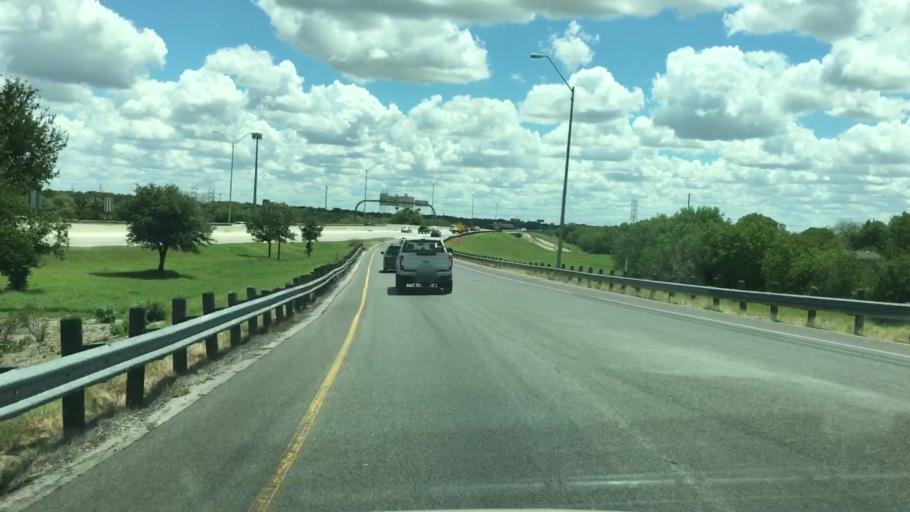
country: US
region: Texas
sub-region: Bexar County
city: China Grove
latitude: 29.3274
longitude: -98.4153
